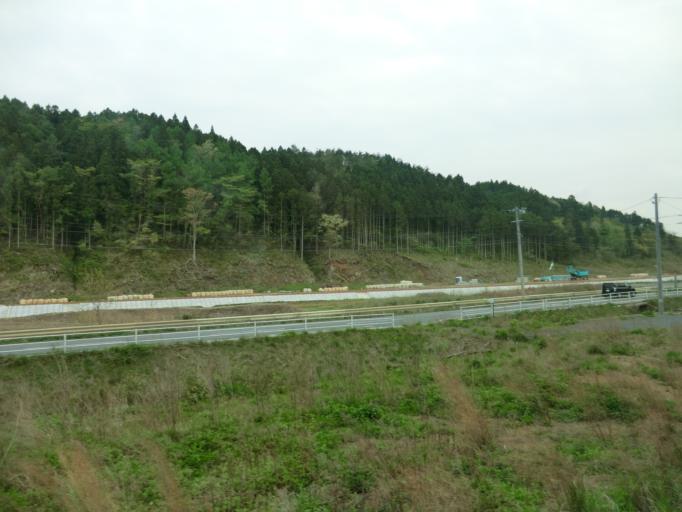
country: JP
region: Miyagi
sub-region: Oshika Gun
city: Onagawa Cho
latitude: 38.6478
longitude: 141.4341
